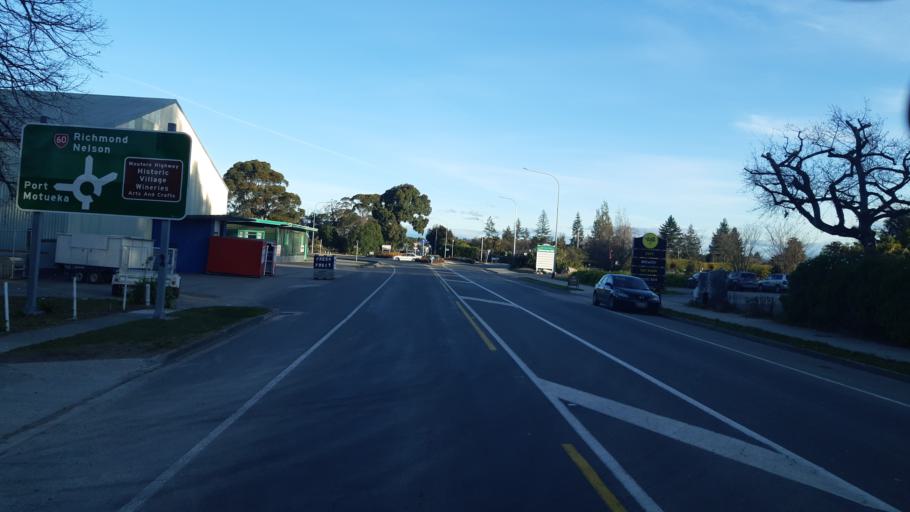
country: NZ
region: Tasman
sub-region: Tasman District
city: Motueka
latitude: -41.1320
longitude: 173.0100
